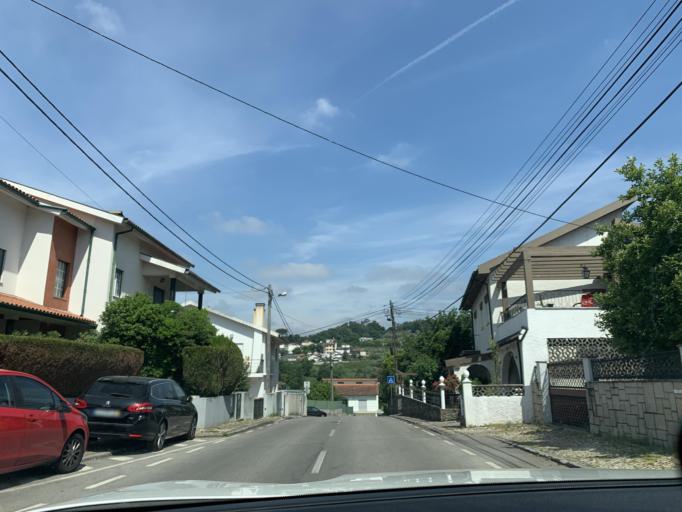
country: PT
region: Viseu
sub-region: Viseu
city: Viseu
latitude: 40.6535
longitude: -7.9345
